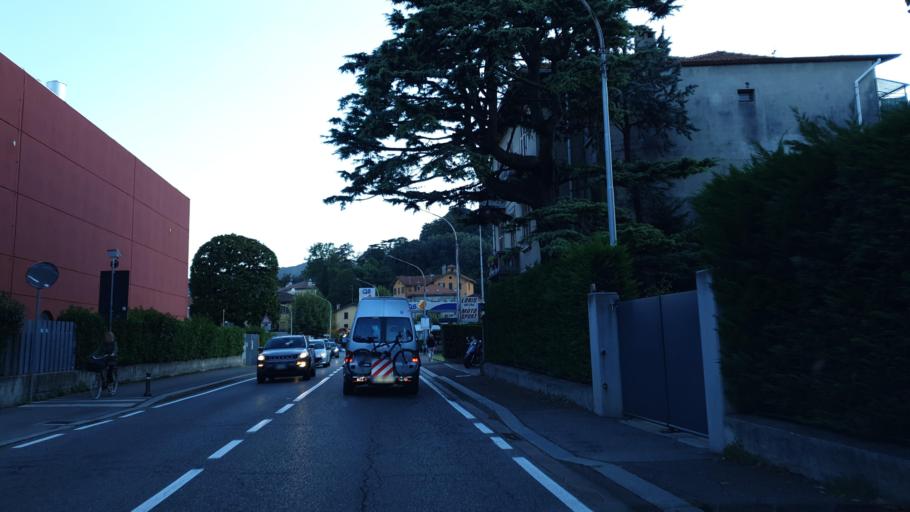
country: IT
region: Lombardy
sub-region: Provincia di Como
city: Cernobbio
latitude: 45.8329
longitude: 9.0720
